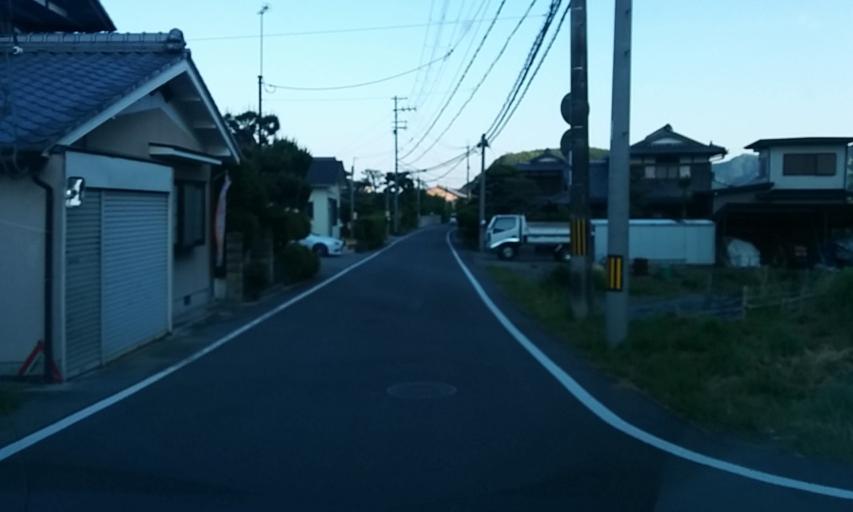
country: JP
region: Kyoto
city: Kameoka
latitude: 35.0923
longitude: 135.5088
